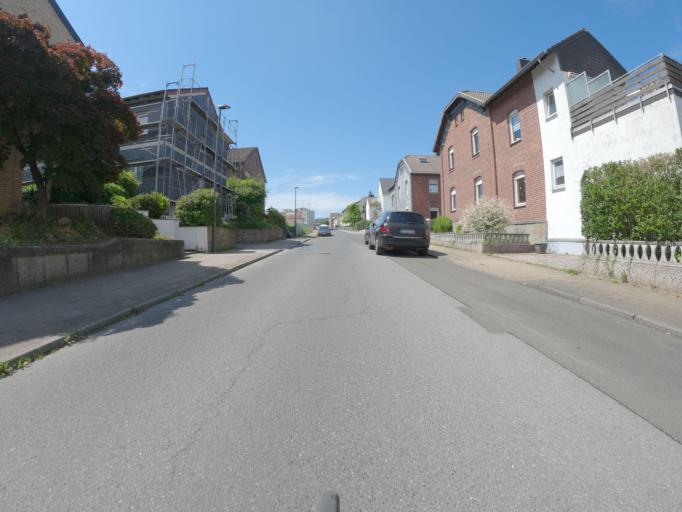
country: DE
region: North Rhine-Westphalia
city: Stolberg
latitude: 50.7489
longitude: 6.1711
